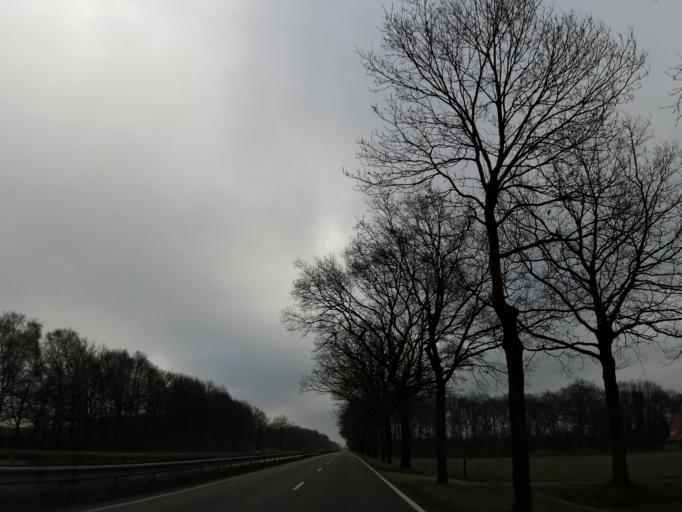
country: NL
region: Limburg
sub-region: Gemeente Leudal
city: Heythuysen
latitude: 51.3236
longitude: 5.8986
